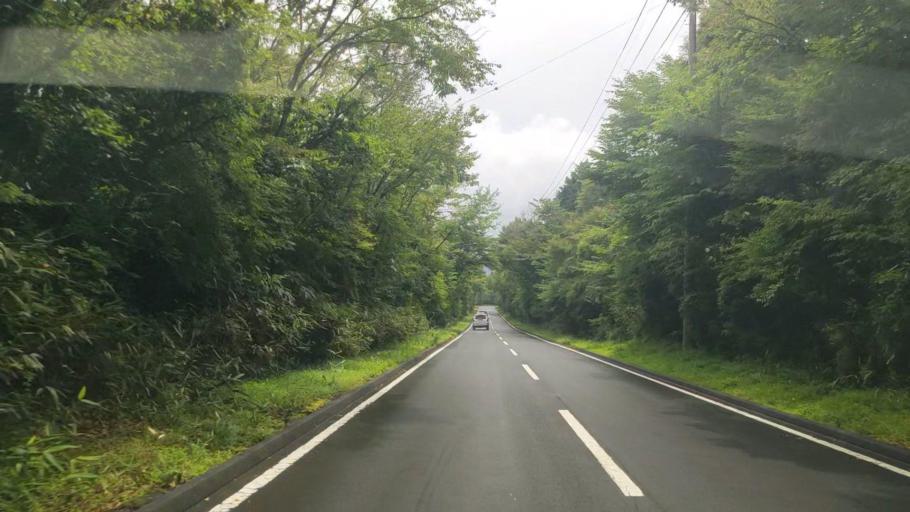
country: JP
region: Shizuoka
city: Gotemba
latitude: 35.2744
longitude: 138.7966
